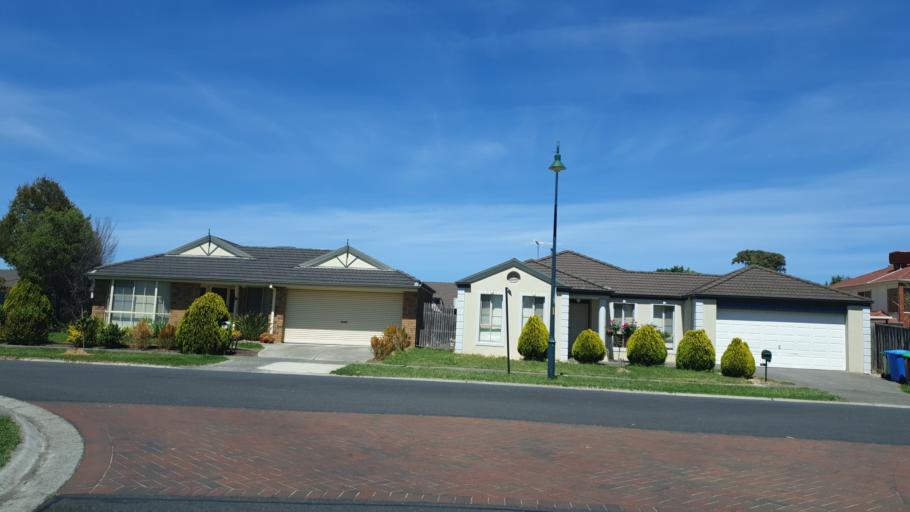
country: AU
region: Victoria
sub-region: Casey
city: Cranbourne North
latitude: -38.0637
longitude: 145.2813
